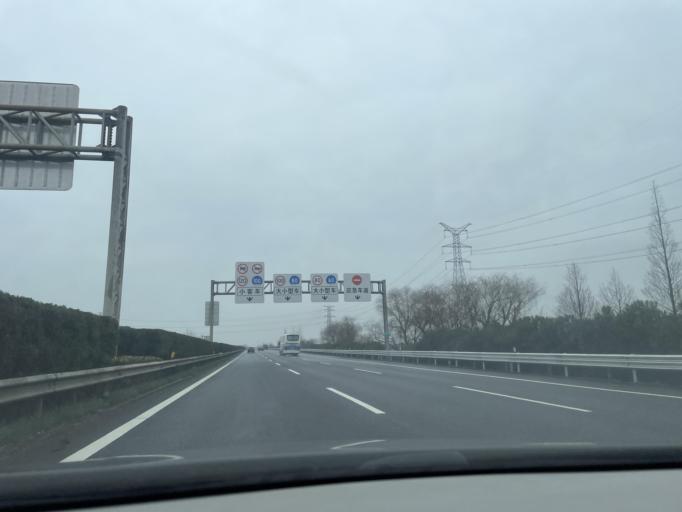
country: CN
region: Zhejiang Sheng
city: Shengshan
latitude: 30.2745
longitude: 121.3116
